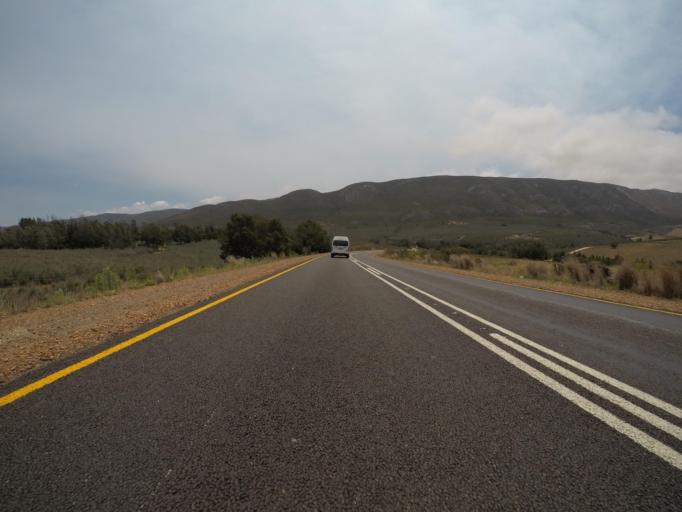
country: ZA
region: Western Cape
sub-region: Eden District Municipality
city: Knysna
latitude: -33.7685
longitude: 22.9618
